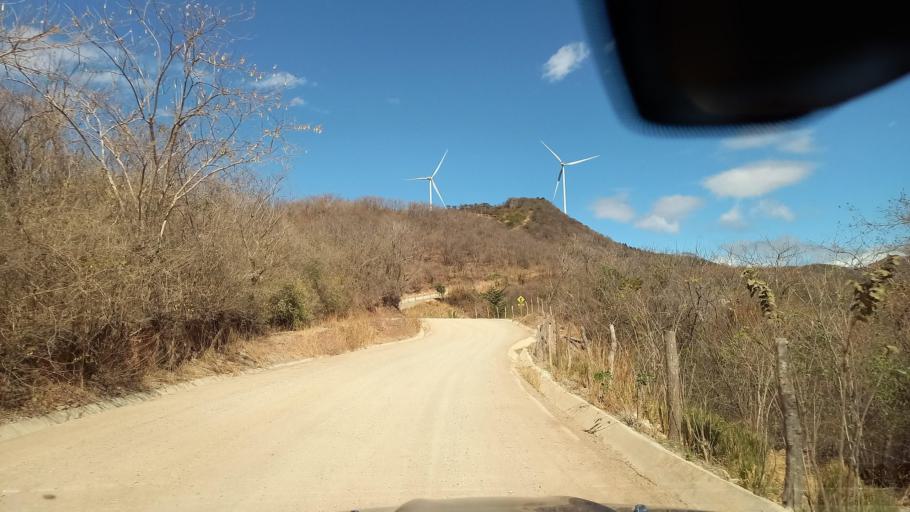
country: SV
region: Santa Ana
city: Metapan
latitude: 14.3584
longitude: -89.4803
